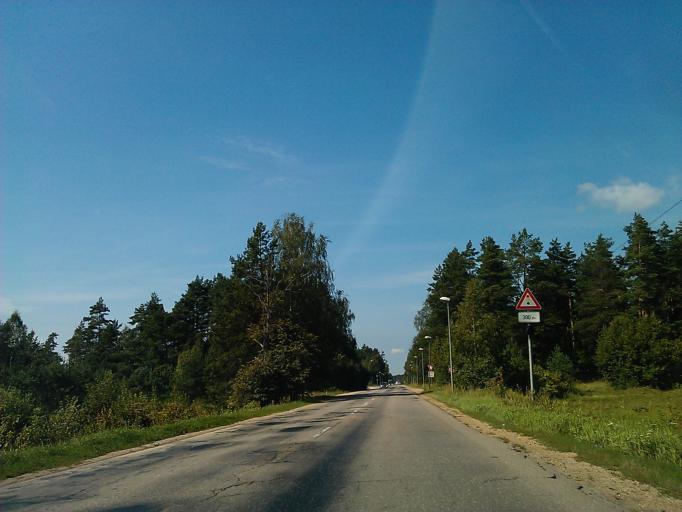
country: LV
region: Salaspils
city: Salaspils
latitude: 56.9419
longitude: 24.3864
